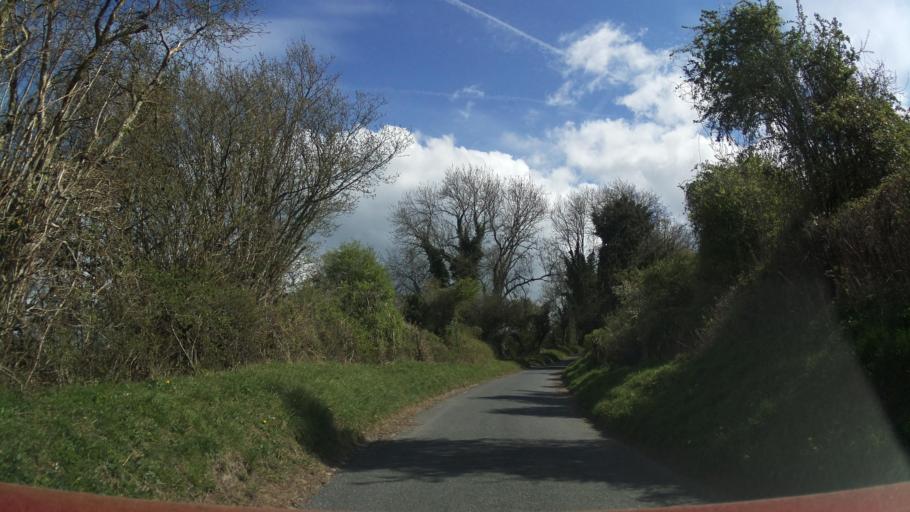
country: GB
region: England
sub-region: West Berkshire
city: Kintbury
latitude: 51.3606
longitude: -1.4756
